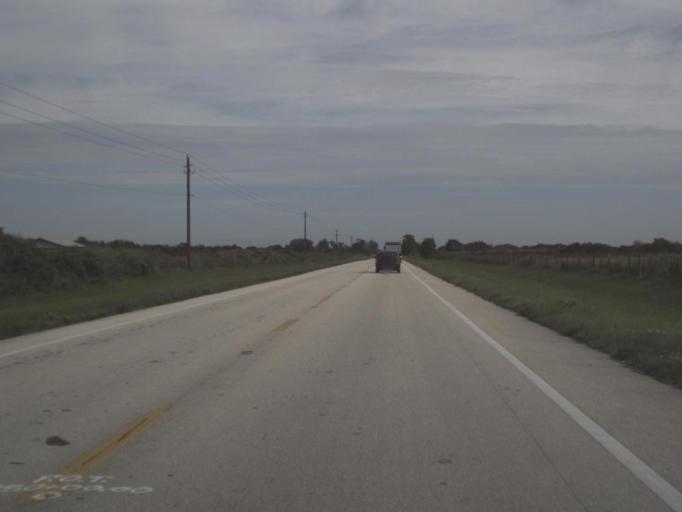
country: US
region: Florida
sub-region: DeSoto County
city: Southeast Arcadia
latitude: 27.0970
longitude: -81.7950
